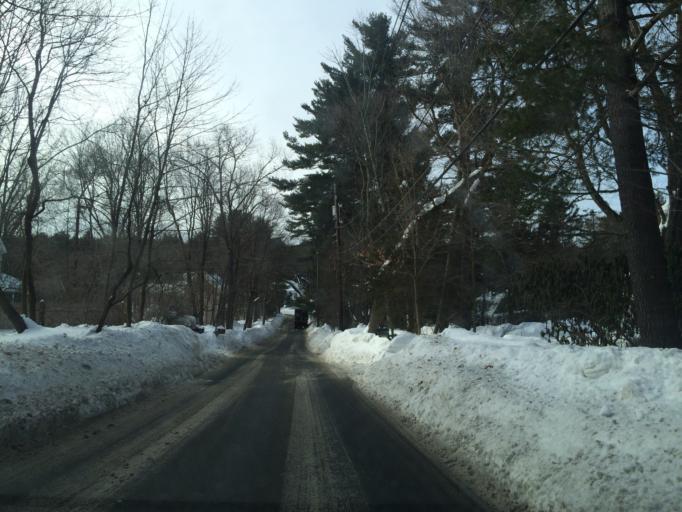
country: US
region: Massachusetts
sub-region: Middlesex County
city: Weston
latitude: 42.3670
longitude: -71.2761
